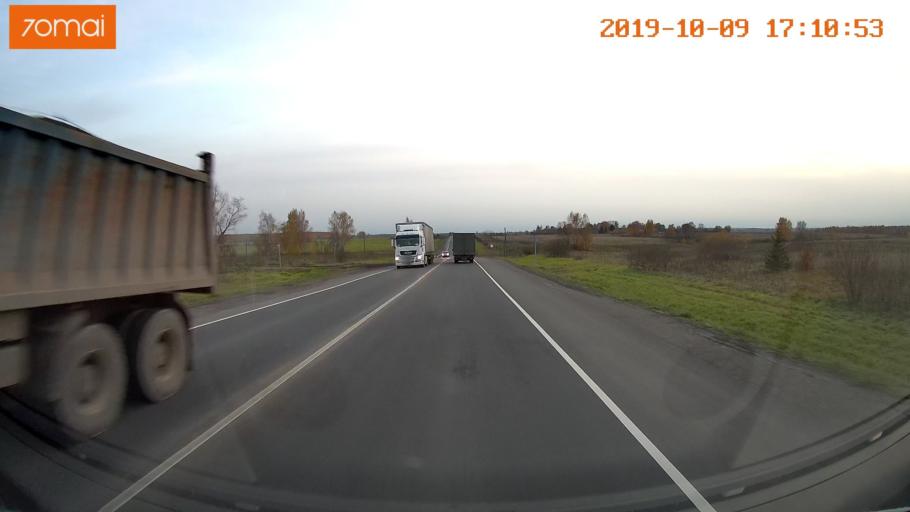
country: RU
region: Ivanovo
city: Privolzhsk
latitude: 57.3497
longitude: 41.2539
